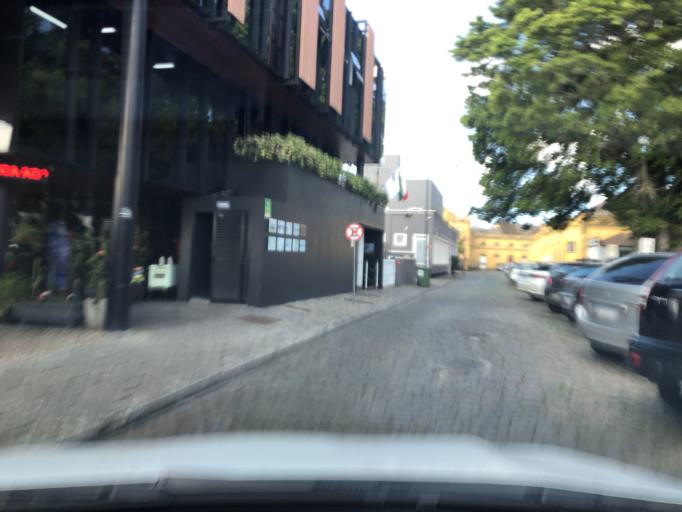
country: BR
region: Santa Catarina
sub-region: Sao Francisco Do Sul
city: Sao Francisco do Sul
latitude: -26.2412
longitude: -48.6402
